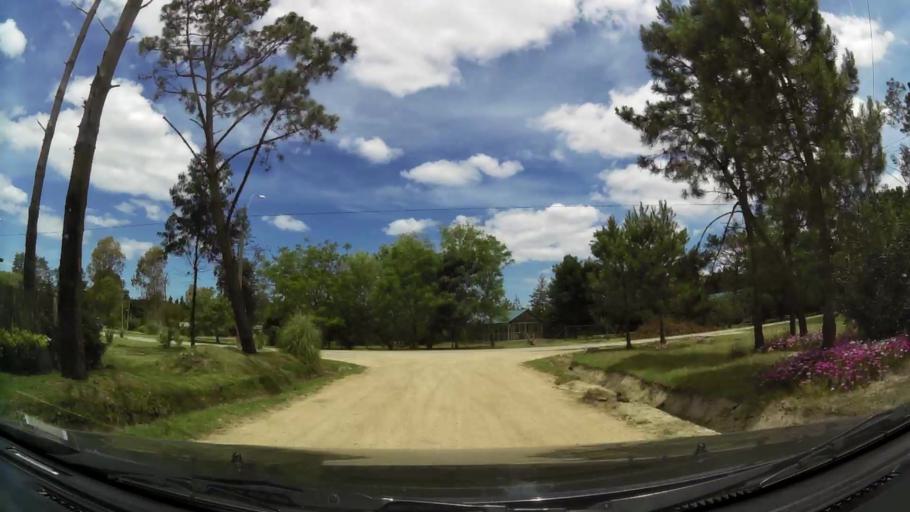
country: UY
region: Canelones
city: Empalme Olmos
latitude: -34.7971
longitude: -55.8893
